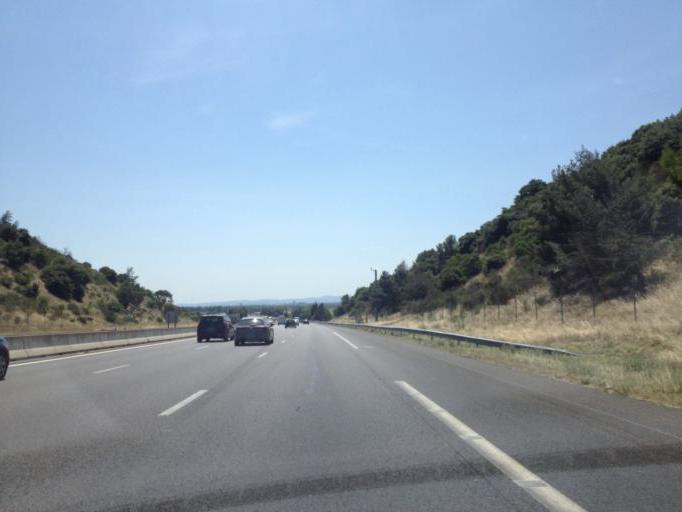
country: FR
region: Rhone-Alpes
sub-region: Departement de la Drome
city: Donzere
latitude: 44.4272
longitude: 4.7386
